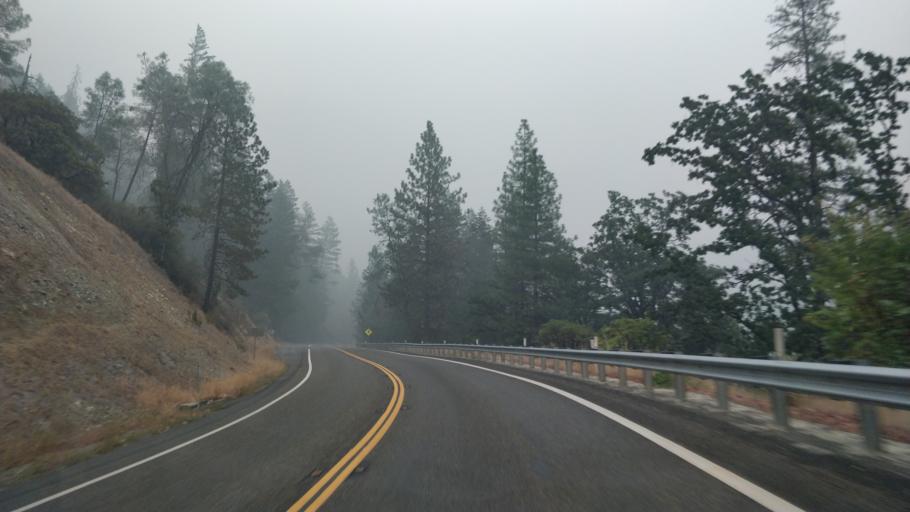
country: US
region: California
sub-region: Trinity County
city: Hayfork
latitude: 40.7825
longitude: -123.3475
